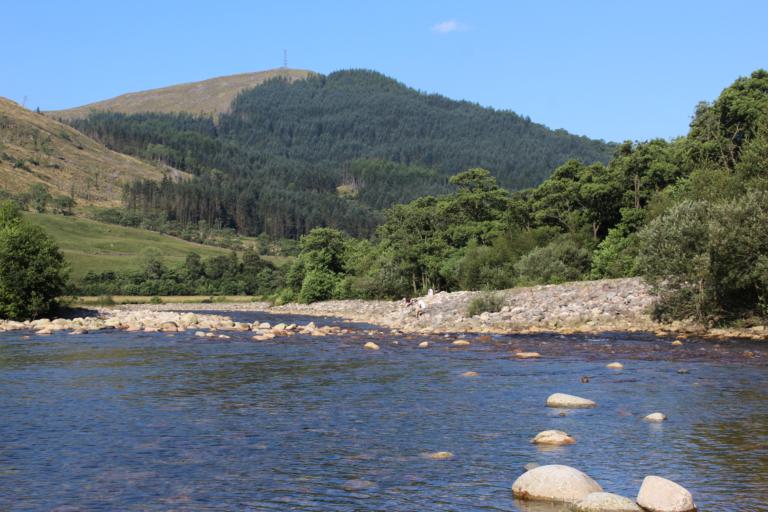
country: GB
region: Scotland
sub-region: Highland
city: Fort William
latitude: 56.6692
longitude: -5.0693
